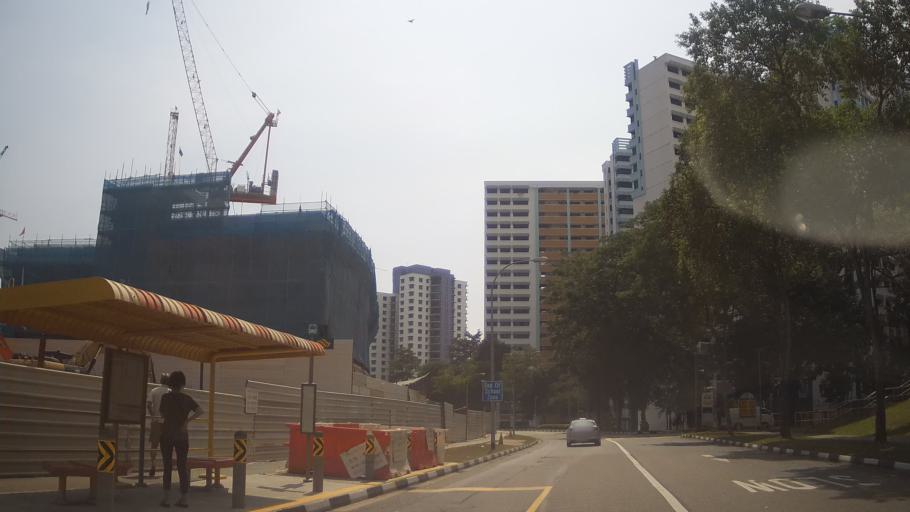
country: MY
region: Johor
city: Johor Bahru
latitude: 1.3869
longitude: 103.7608
